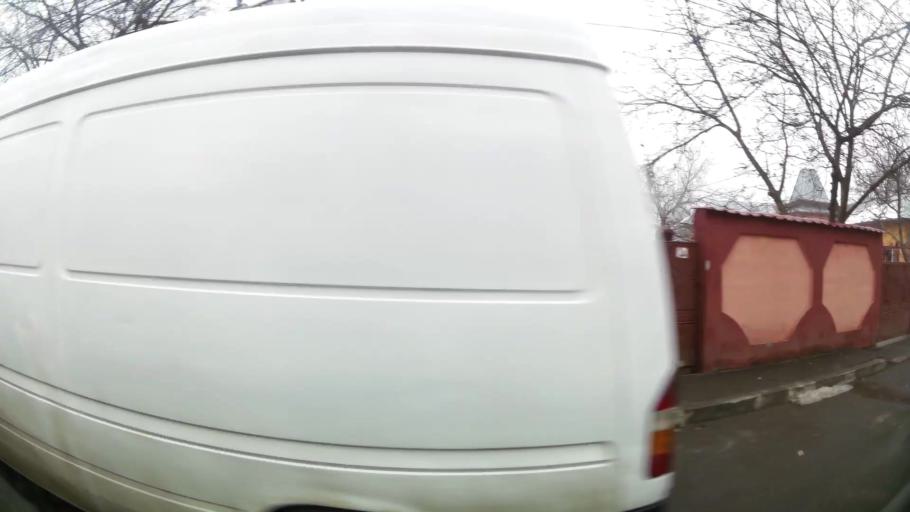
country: RO
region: Ilfov
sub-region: Comuna Chiajna
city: Rosu
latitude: 44.4711
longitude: 26.0085
